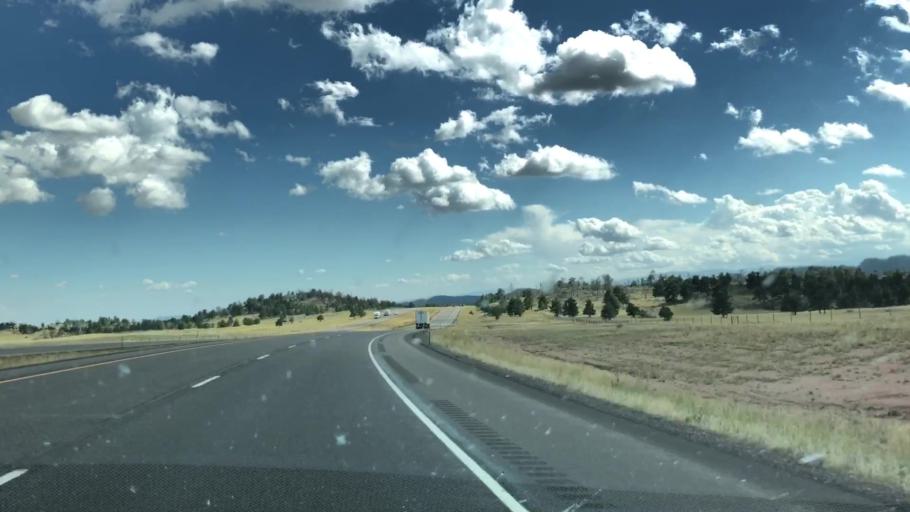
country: US
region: Wyoming
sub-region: Albany County
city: Laramie
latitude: 41.0191
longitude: -105.4214
